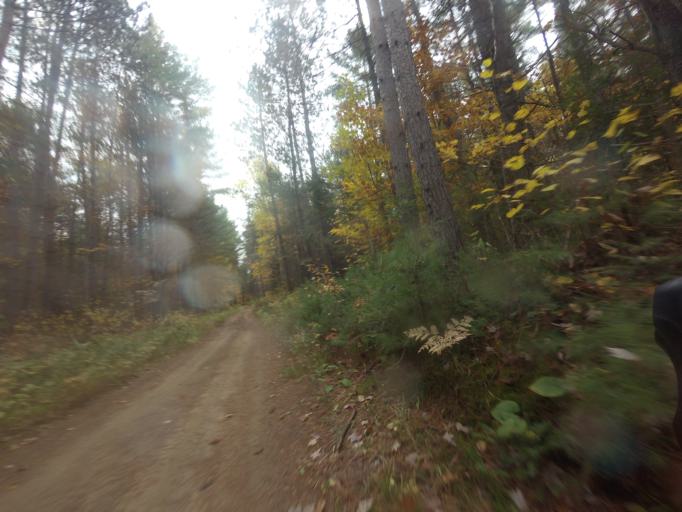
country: CA
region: Ontario
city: Petawawa
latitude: 45.7735
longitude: -77.3742
